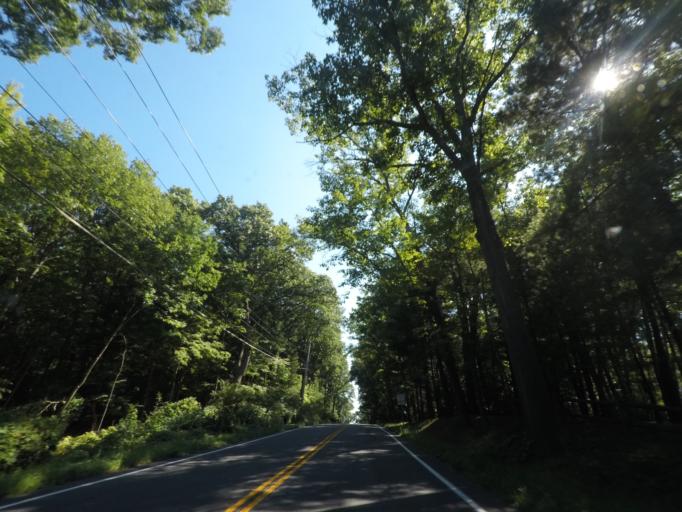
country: US
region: New York
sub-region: Albany County
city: Menands
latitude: 42.7055
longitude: -73.7422
